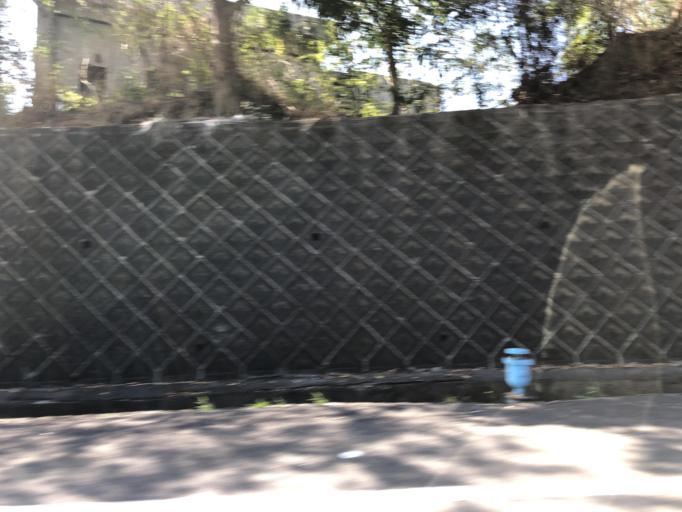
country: TW
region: Taiwan
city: Yujing
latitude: 23.0581
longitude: 120.3974
